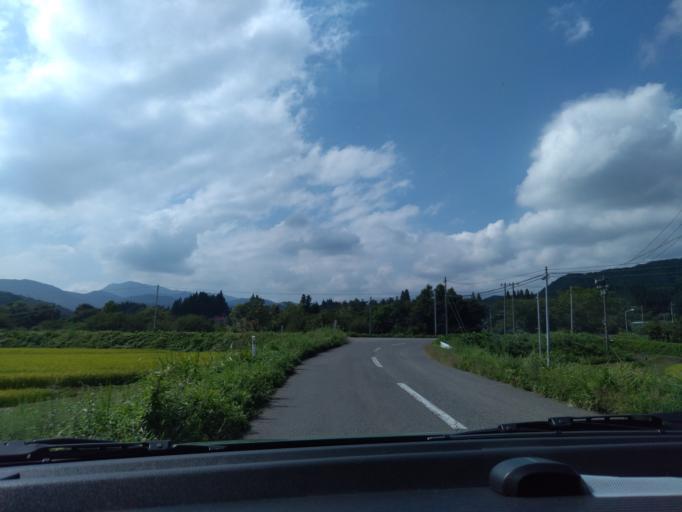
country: JP
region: Iwate
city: Shizukuishi
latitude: 39.6836
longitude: 140.9129
